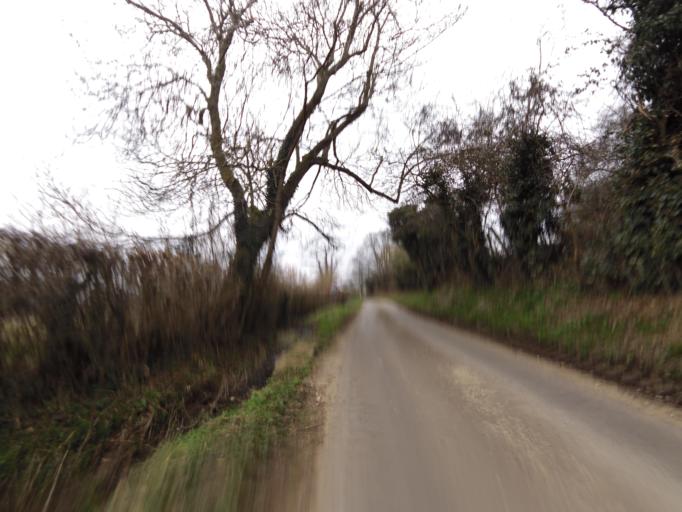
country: GB
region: England
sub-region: Suffolk
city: Framlingham
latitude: 52.2453
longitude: 1.4037
